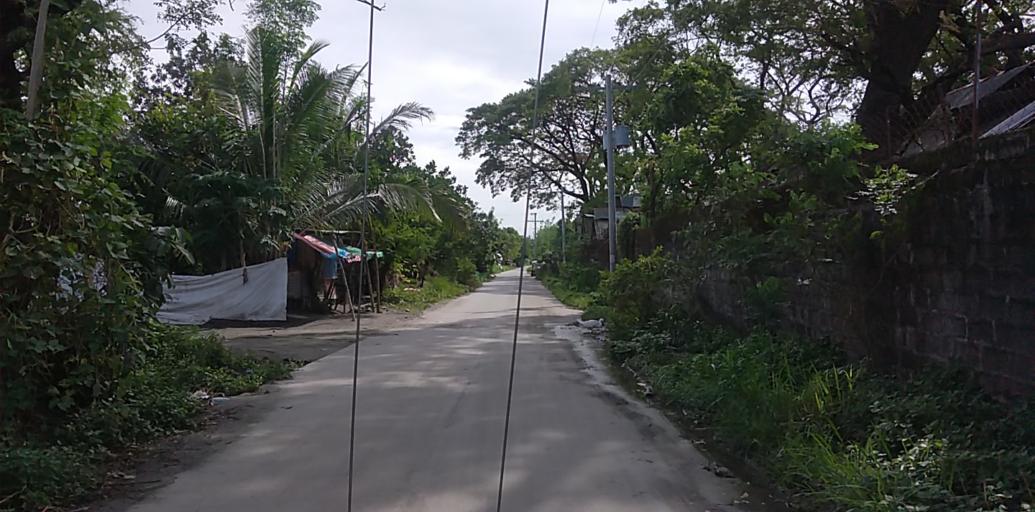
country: PH
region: Central Luzon
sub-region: Province of Pampanga
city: Angeles City
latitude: 15.1295
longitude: 120.5611
